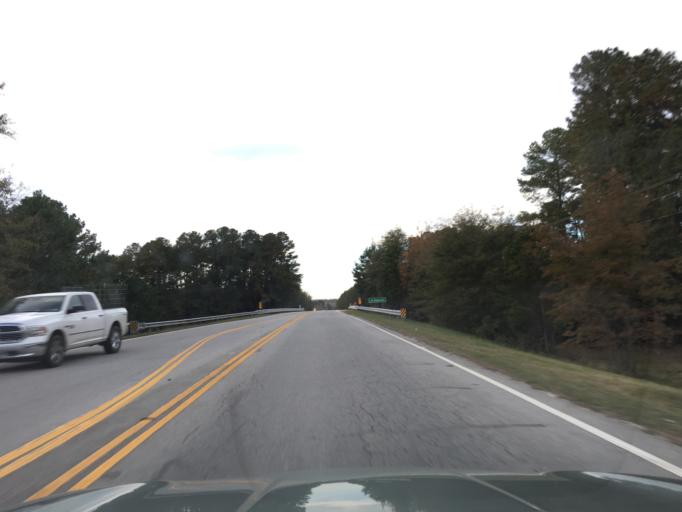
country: US
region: South Carolina
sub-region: Lexington County
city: Leesville
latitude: 33.8155
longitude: -81.4509
